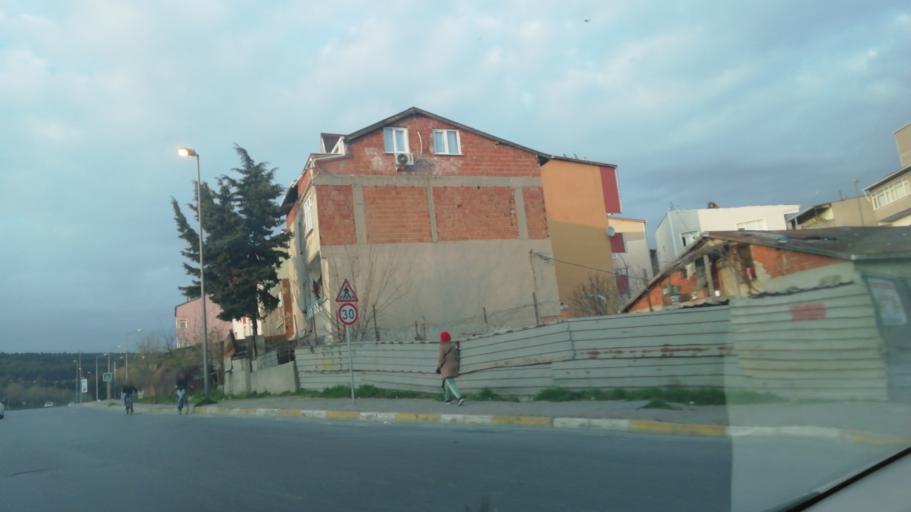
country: TR
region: Istanbul
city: Mahmutbey
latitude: 41.0192
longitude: 28.7818
